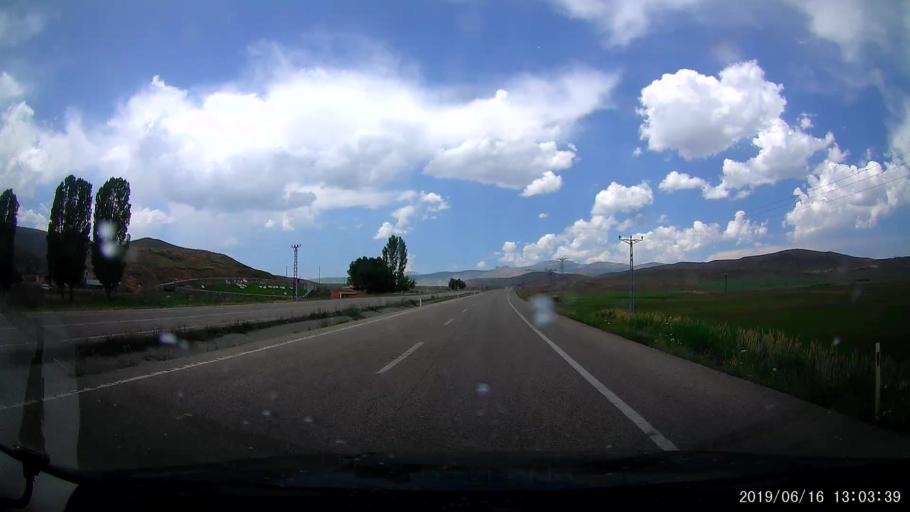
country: TR
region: Agri
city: Sulucem
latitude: 39.5837
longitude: 43.7864
